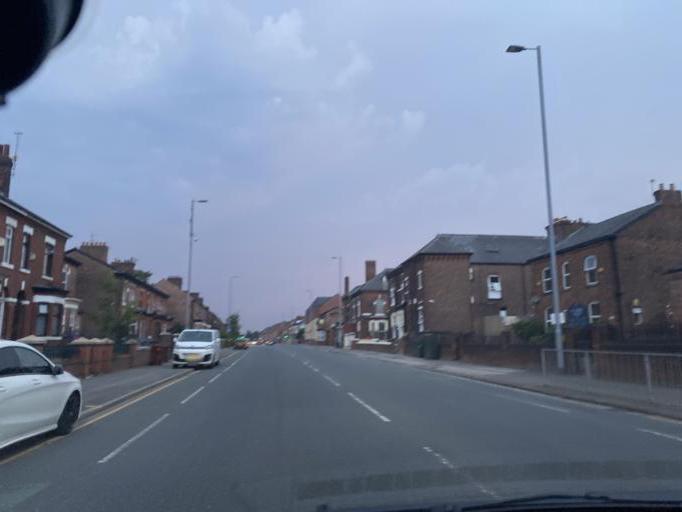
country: GB
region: England
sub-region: Borough of Tameside
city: Droylsden
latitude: 53.4726
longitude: -2.1519
